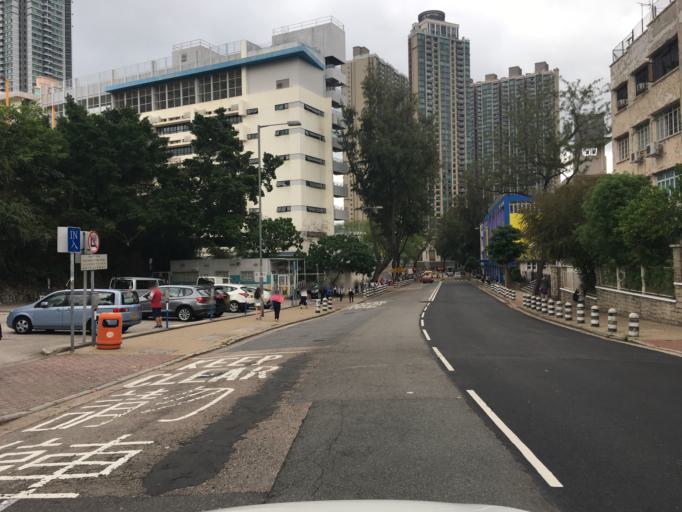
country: HK
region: Kowloon City
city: Kowloon
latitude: 22.3224
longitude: 114.1846
